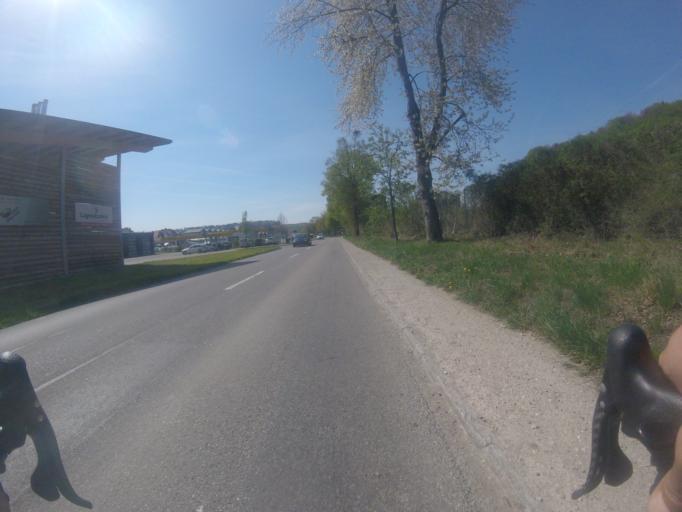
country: CH
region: Bern
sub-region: Bern-Mittelland District
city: Laupen
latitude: 46.9092
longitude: 7.2356
